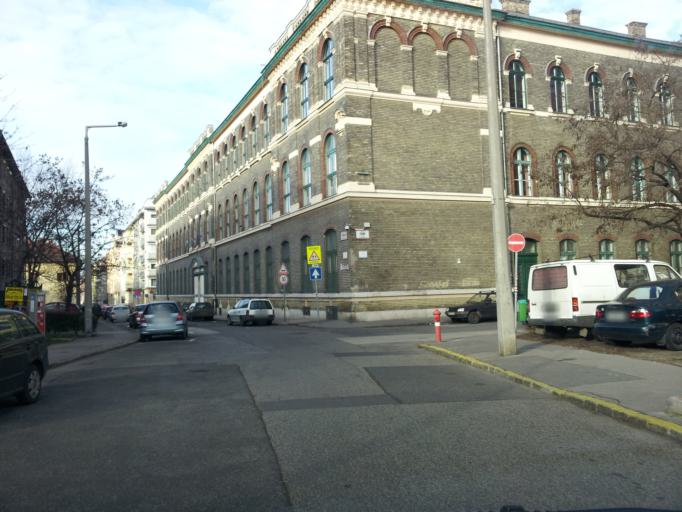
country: HU
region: Budapest
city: Budapest VIII. keruelet
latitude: 47.4780
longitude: 19.0840
